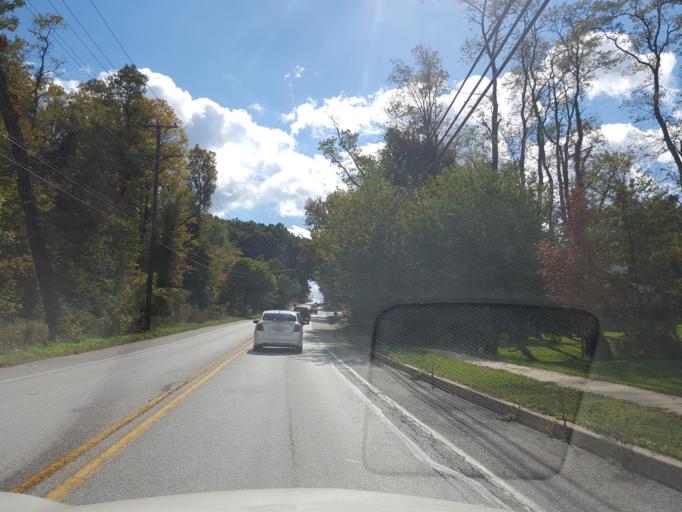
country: US
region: Pennsylvania
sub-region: York County
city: Stonybrook
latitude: 39.9671
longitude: -76.6596
